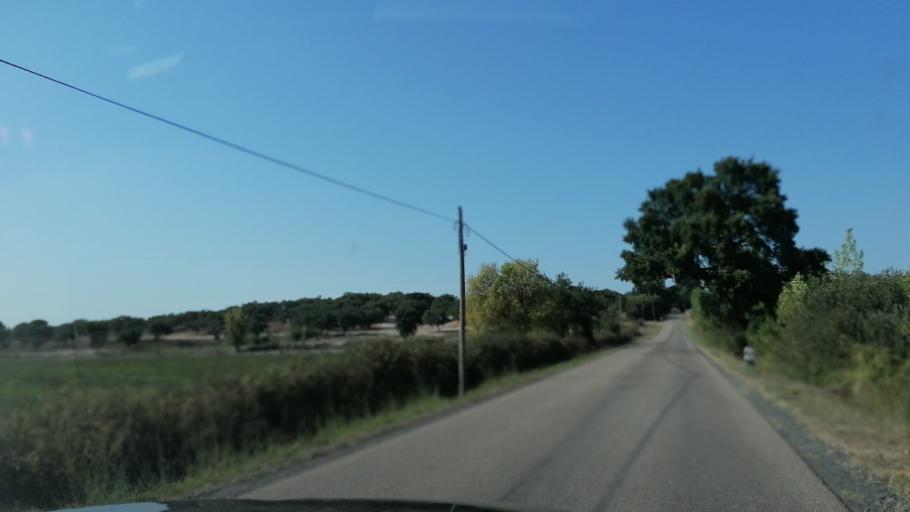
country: PT
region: Santarem
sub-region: Coruche
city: Coruche
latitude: 38.7987
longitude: -8.5788
